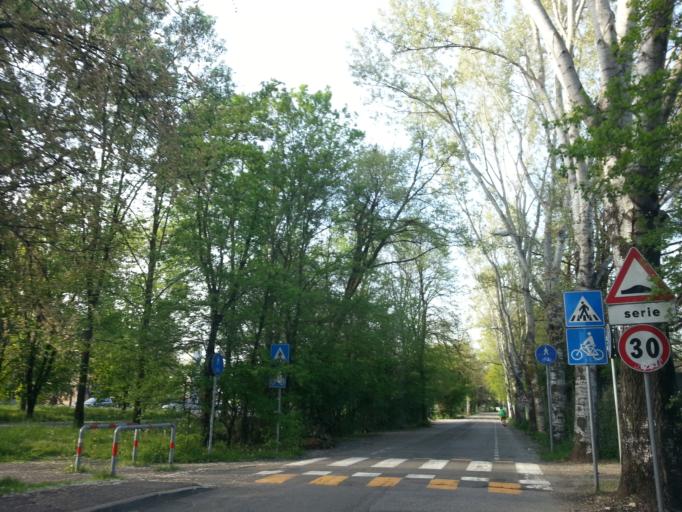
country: IT
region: Emilia-Romagna
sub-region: Provincia di Reggio Emilia
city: Forche
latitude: 44.6631
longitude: 10.5902
